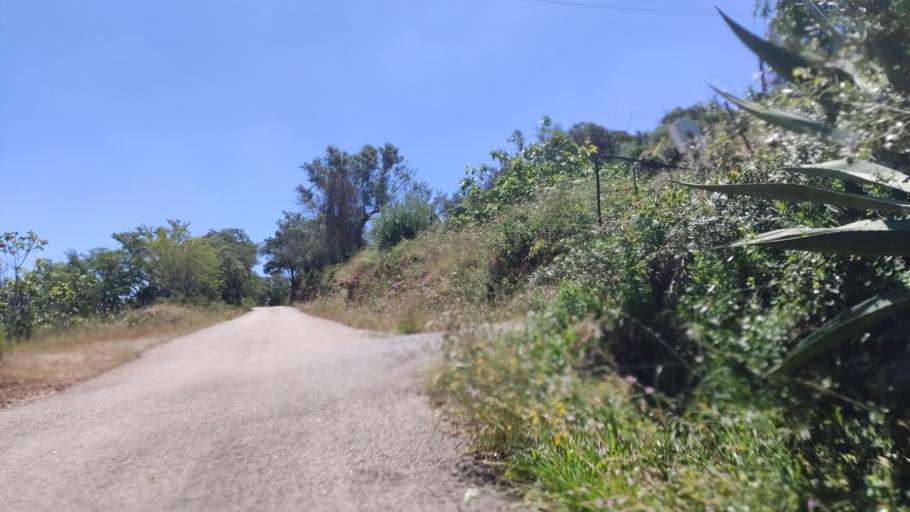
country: PT
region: Faro
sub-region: Sao Bras de Alportel
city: Sao Bras de Alportel
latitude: 37.1729
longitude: -7.9158
